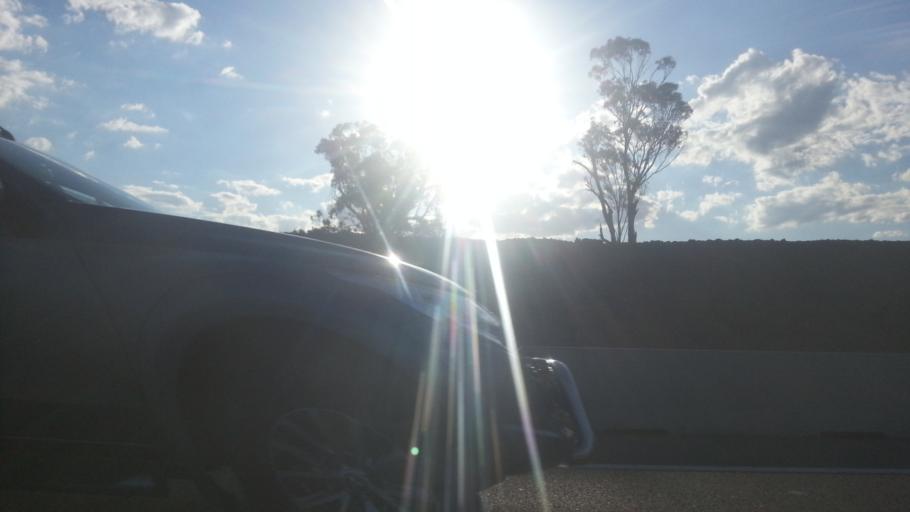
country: AU
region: New South Wales
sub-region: Liverpool
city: Bringelly
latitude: -33.9607
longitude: 150.7388
